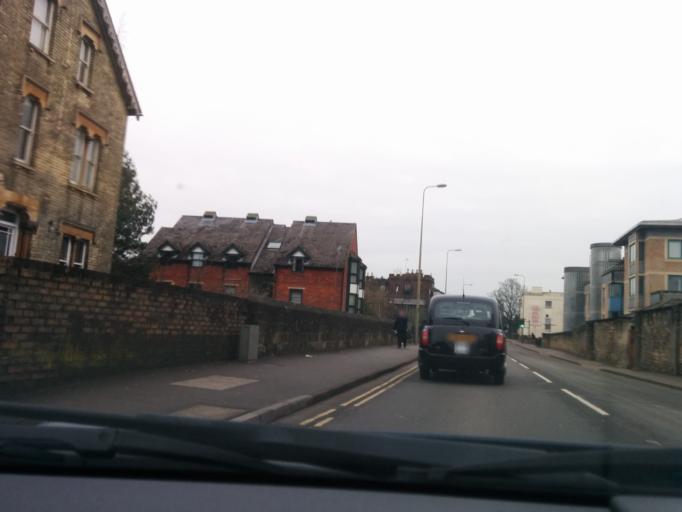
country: GB
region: England
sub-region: Oxfordshire
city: Oxford
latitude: 51.7450
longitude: -1.2562
